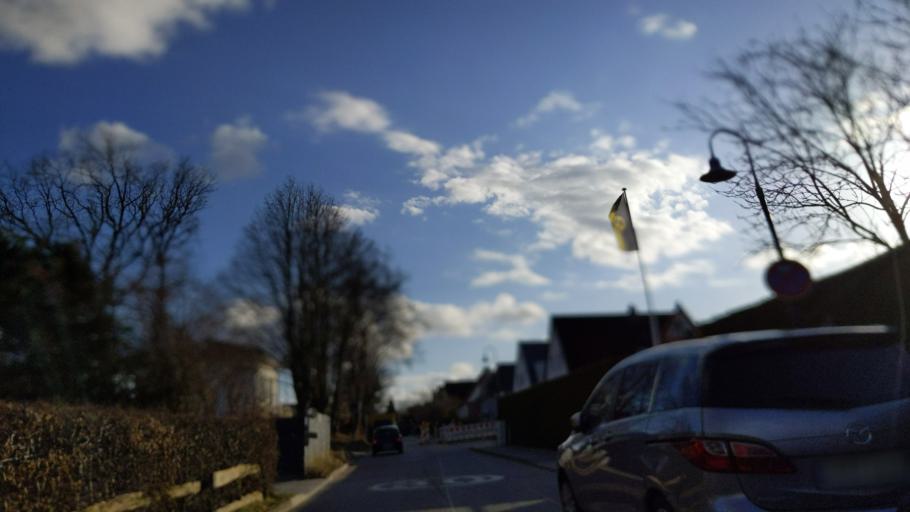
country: DE
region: Schleswig-Holstein
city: Scharbeutz
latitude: 54.0332
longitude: 10.7435
